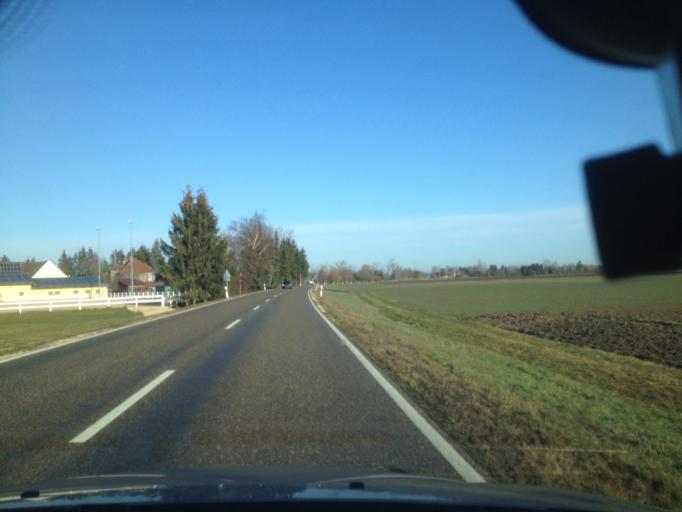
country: DE
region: Bavaria
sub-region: Swabia
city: Offingen
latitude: 48.5028
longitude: 10.3613
